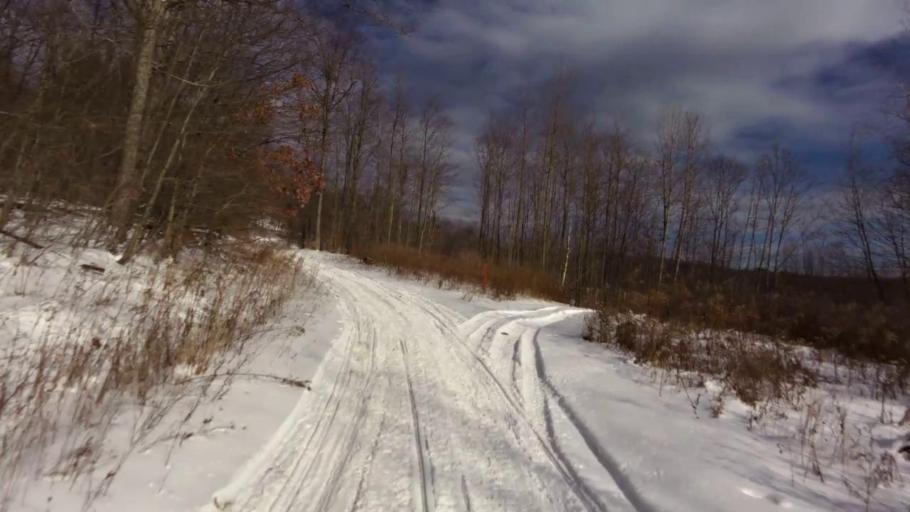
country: US
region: Pennsylvania
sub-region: McKean County
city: Foster Brook
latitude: 42.0043
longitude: -78.6144
